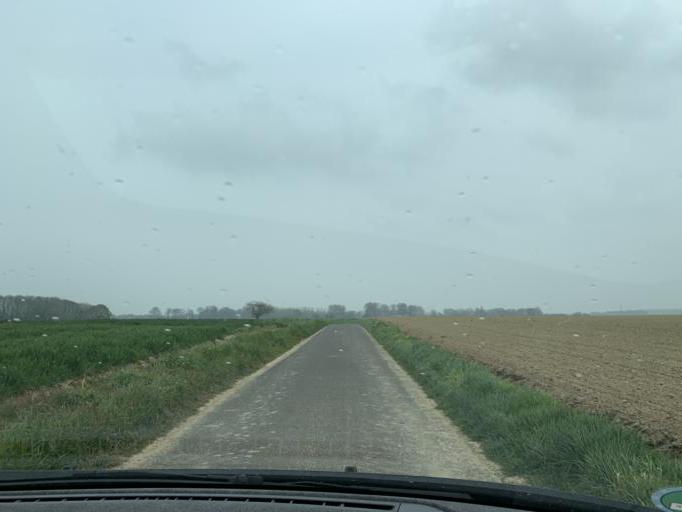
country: FR
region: Haute-Normandie
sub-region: Departement de la Seine-Maritime
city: Fontaine-le-Dun
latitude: 49.8583
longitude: 0.8324
